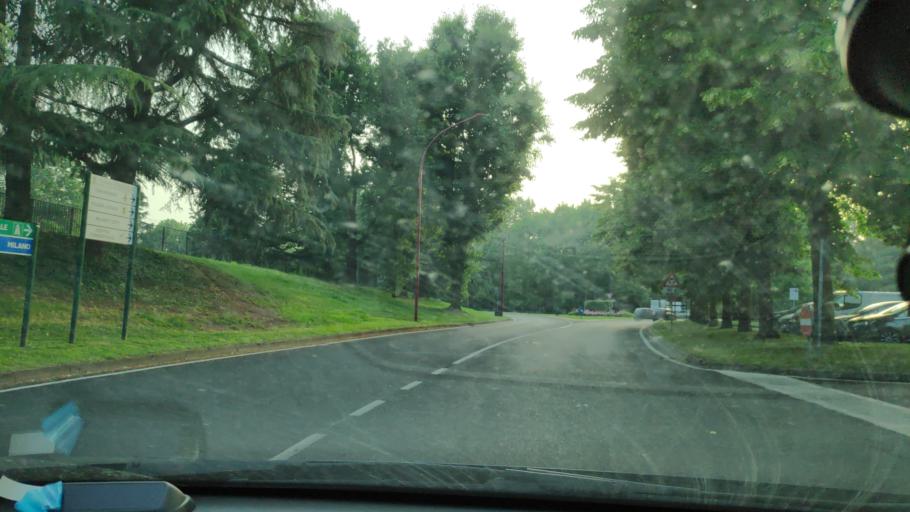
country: IT
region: Lombardy
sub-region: Citta metropolitana di Milano
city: Basiglio
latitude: 45.3609
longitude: 9.1580
